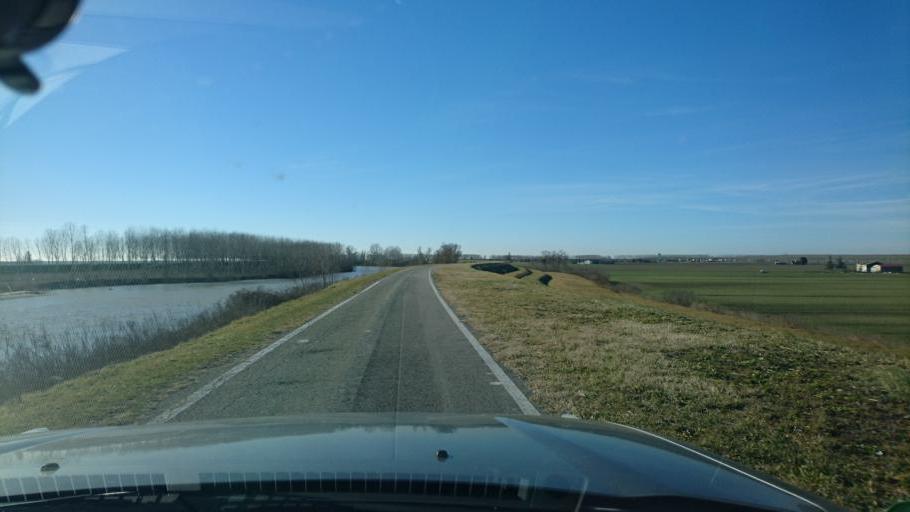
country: IT
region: Veneto
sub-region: Provincia di Rovigo
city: Ariano
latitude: 44.9316
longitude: 12.1560
